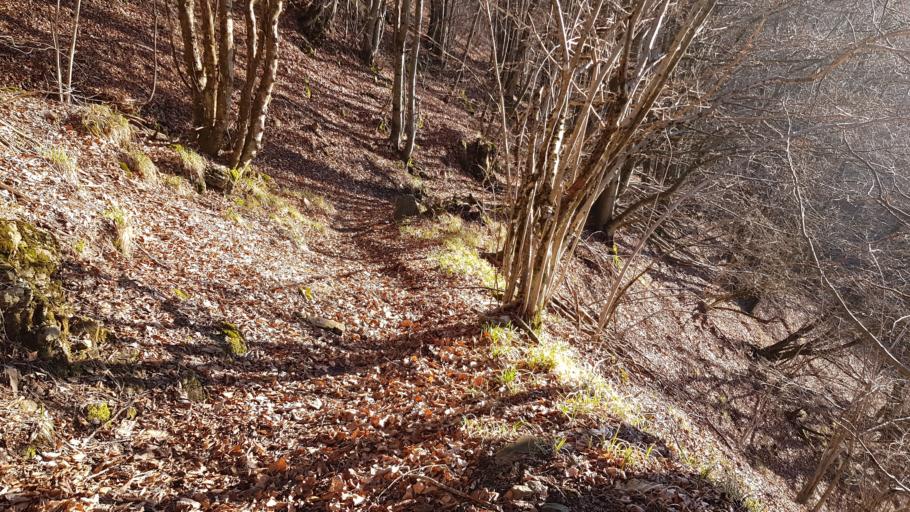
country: IT
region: Liguria
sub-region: Provincia di Genova
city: Torriglia
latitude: 44.5413
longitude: 9.1552
